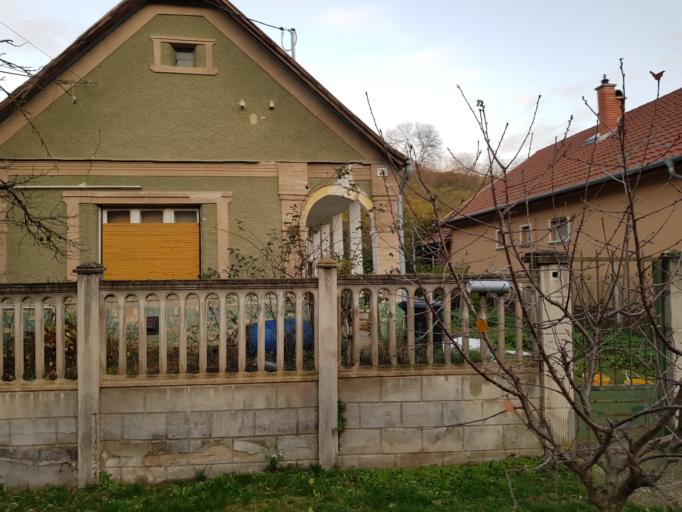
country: HU
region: Pest
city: Gomba
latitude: 47.3509
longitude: 19.5393
